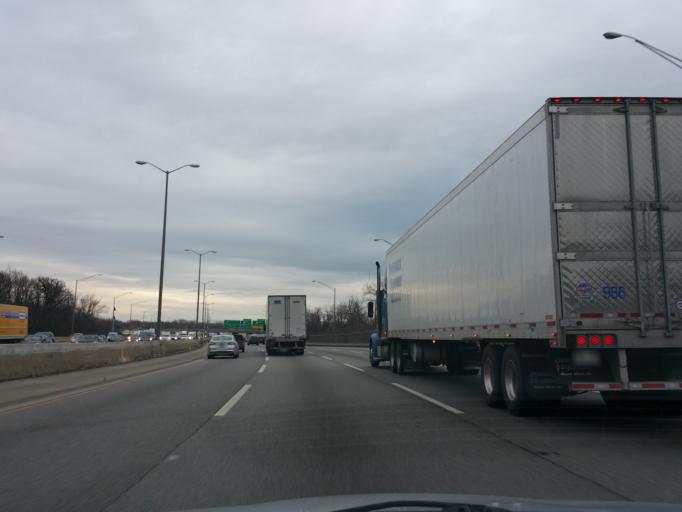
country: US
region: Illinois
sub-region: DuPage County
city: Oak Brook
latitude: 41.8252
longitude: -87.9180
